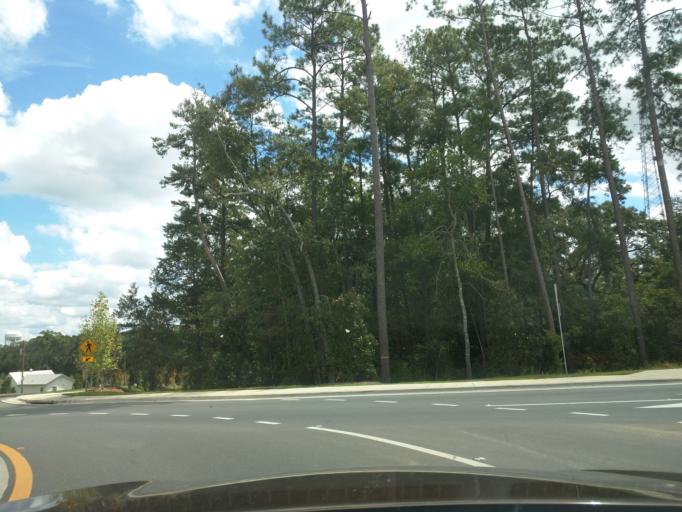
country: US
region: Florida
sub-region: Leon County
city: Tallahassee
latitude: 30.5631
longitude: -84.2195
